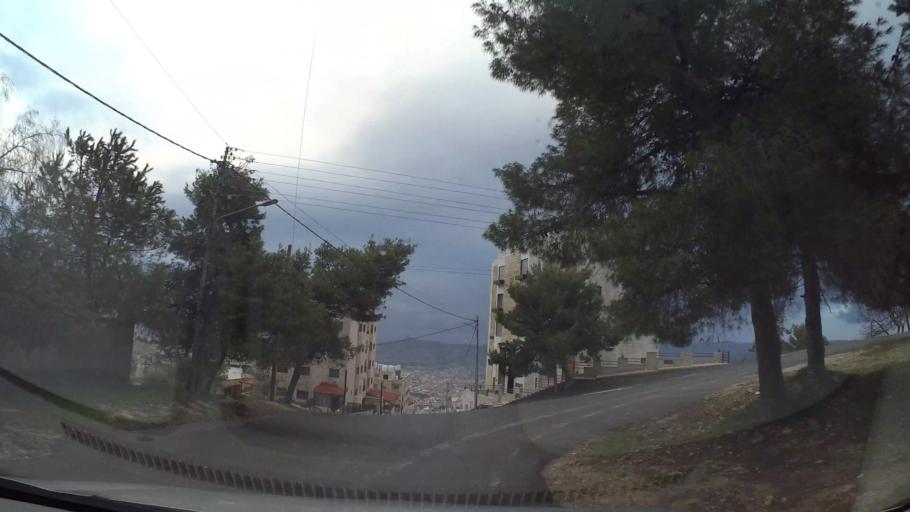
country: JO
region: Amman
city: Al Jubayhah
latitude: 32.0313
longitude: 35.8291
